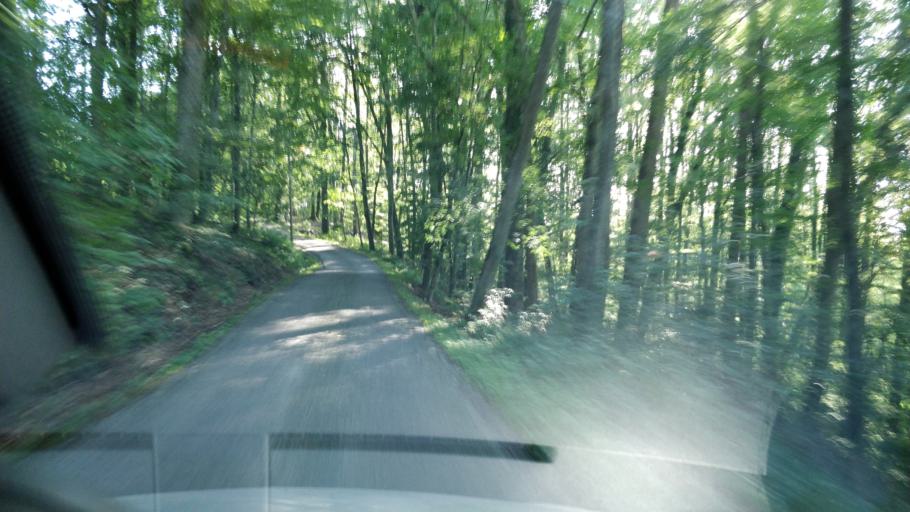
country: DE
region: Baden-Wuerttemberg
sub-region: Regierungsbezirk Stuttgart
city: Murrhardt
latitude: 49.0155
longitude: 9.5850
